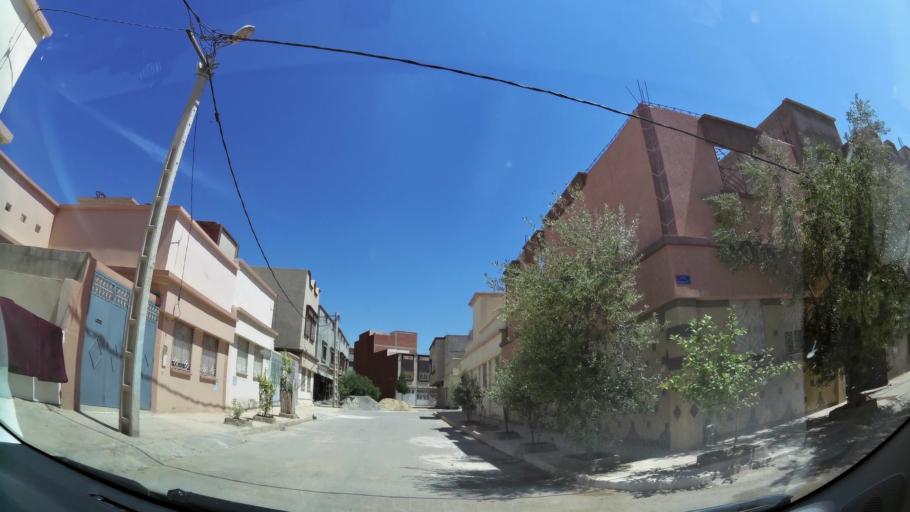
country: MA
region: Oriental
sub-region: Oujda-Angad
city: Oujda
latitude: 34.6854
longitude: -1.9490
